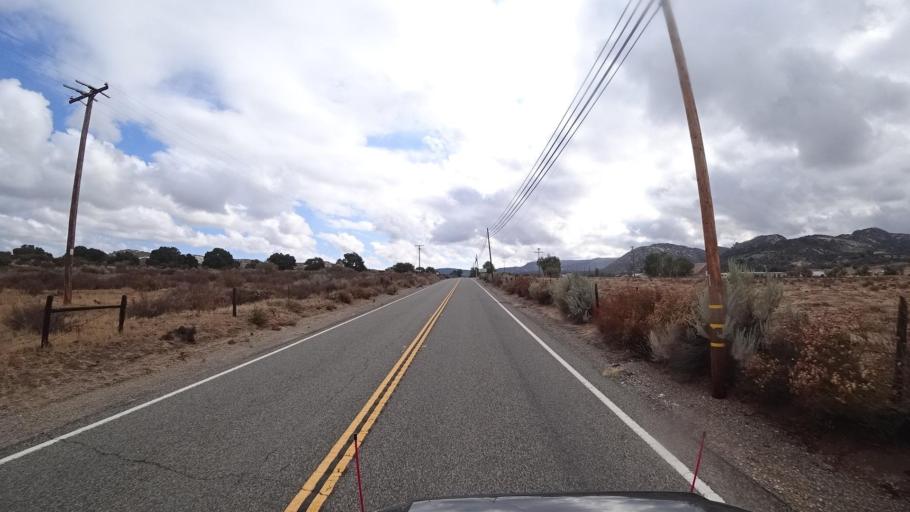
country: US
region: California
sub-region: San Diego County
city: Campo
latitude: 32.6301
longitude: -116.4471
